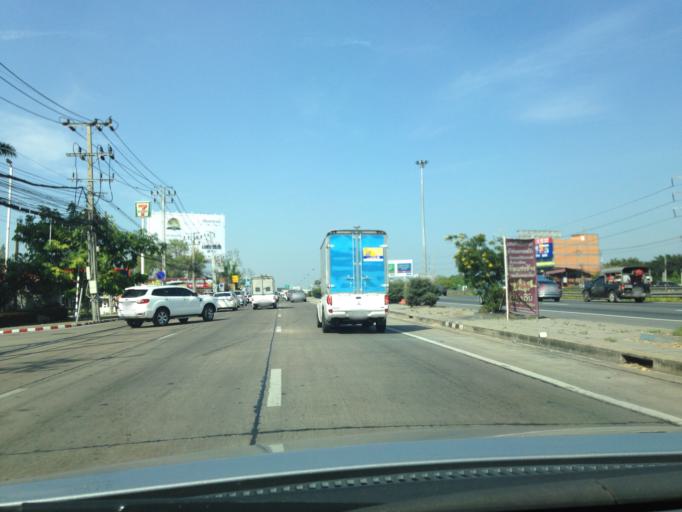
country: TH
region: Nonthaburi
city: Bang Yai
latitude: 13.8251
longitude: 100.4125
